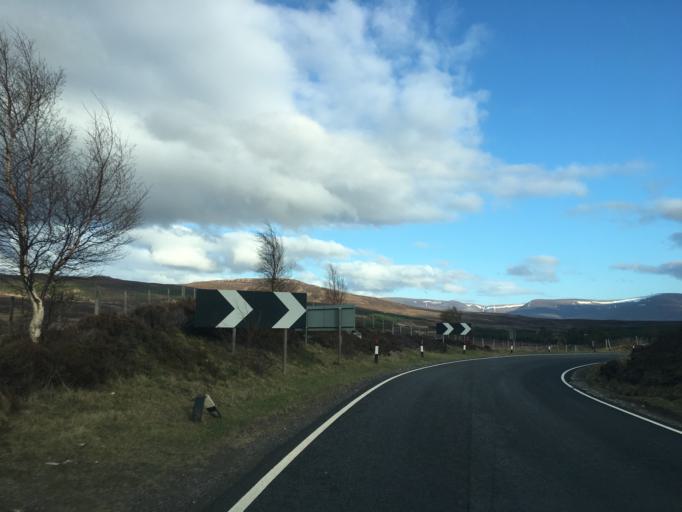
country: GB
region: Scotland
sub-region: Highland
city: Kingussie
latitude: 56.9973
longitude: -4.2492
